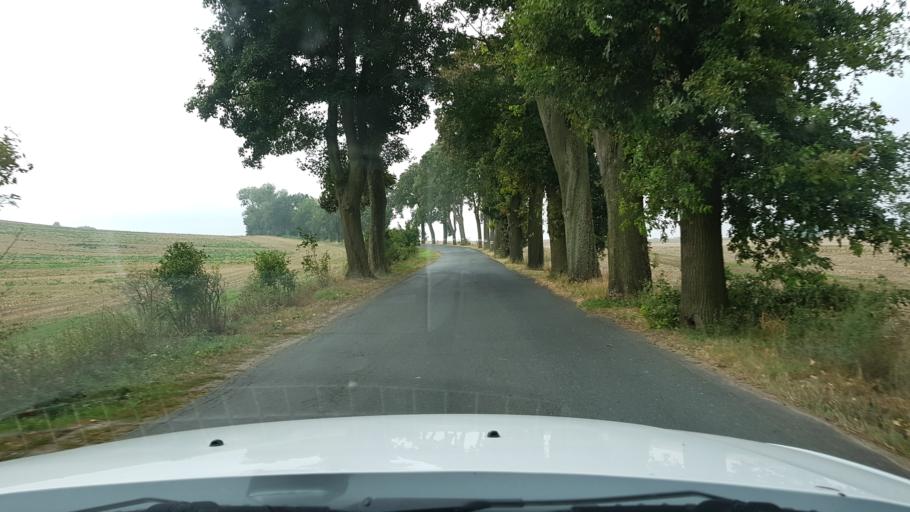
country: PL
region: West Pomeranian Voivodeship
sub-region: Powiat gryfinski
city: Moryn
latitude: 52.8874
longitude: 14.3778
